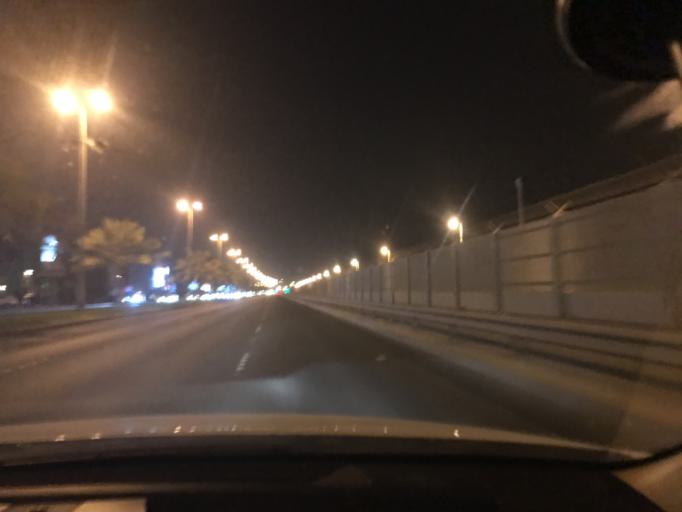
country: BH
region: Muharraq
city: Al Hadd
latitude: 26.2580
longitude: 50.6482
